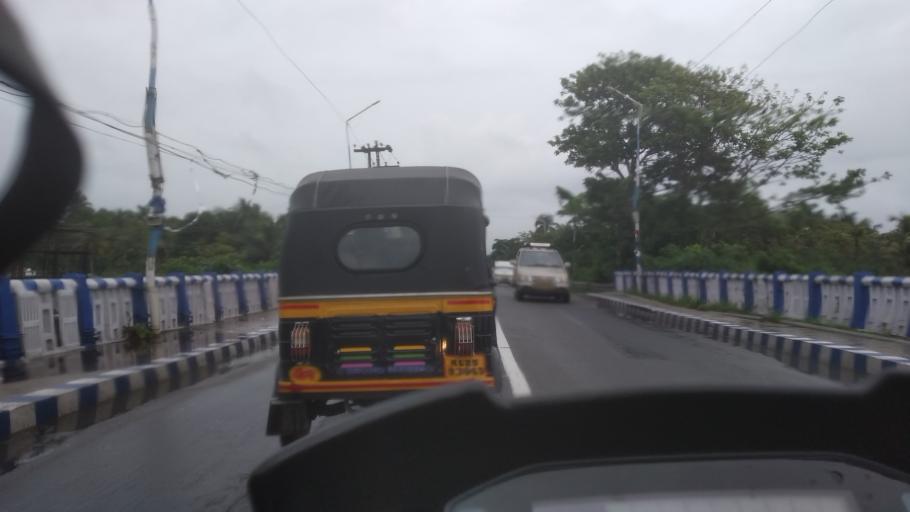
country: IN
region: Kerala
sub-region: Alappuzha
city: Kayankulam
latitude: 9.1734
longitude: 76.4965
